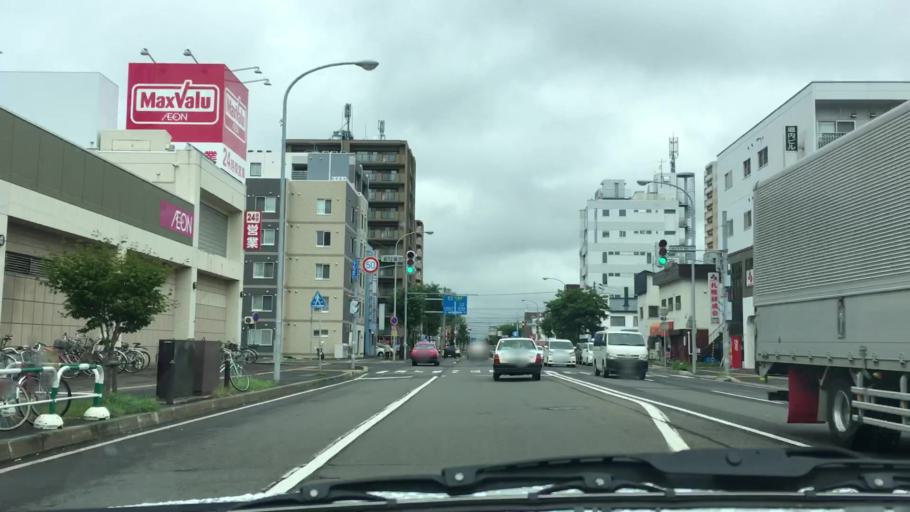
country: JP
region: Hokkaido
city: Sapporo
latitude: 43.0788
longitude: 141.3643
